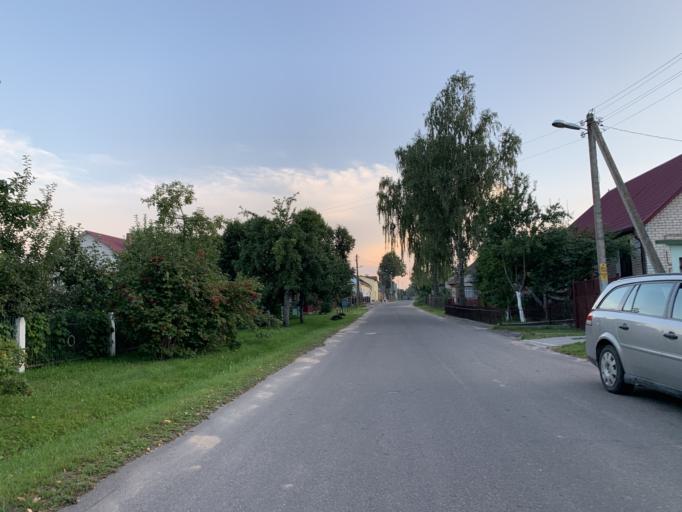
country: BY
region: Minsk
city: Nyasvizh
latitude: 53.2187
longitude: 26.6941
